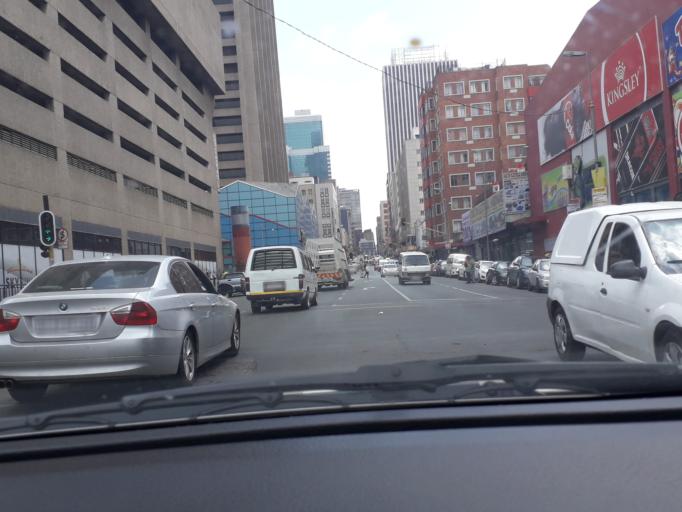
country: ZA
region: Gauteng
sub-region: City of Johannesburg Metropolitan Municipality
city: Johannesburg
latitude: -26.2070
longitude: 28.0478
